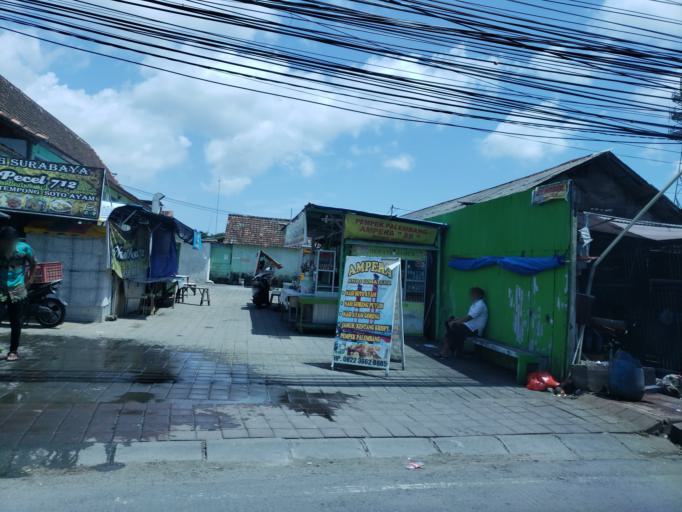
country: ID
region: Bali
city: Jimbaran
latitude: -8.7751
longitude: 115.1716
